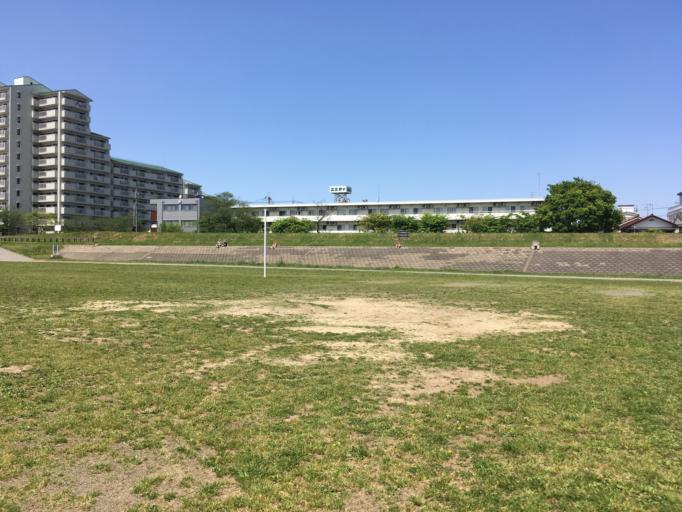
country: JP
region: Tokyo
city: Chofugaoka
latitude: 35.6236
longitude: 139.5743
